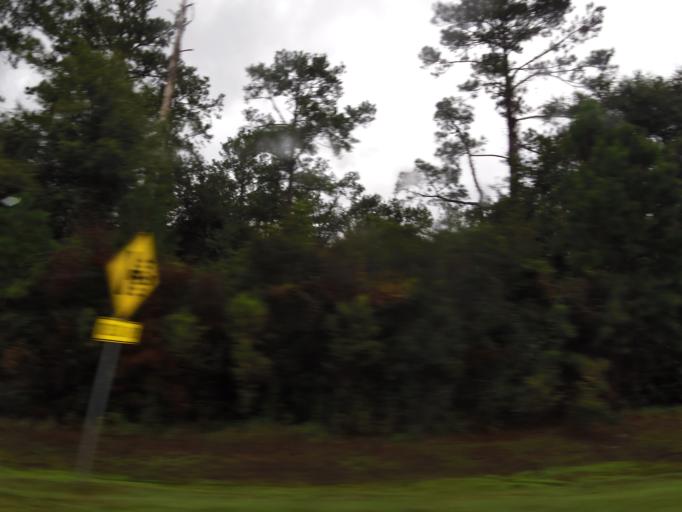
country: US
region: Georgia
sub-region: Wayne County
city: Jesup
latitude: 31.5550
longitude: -81.8201
